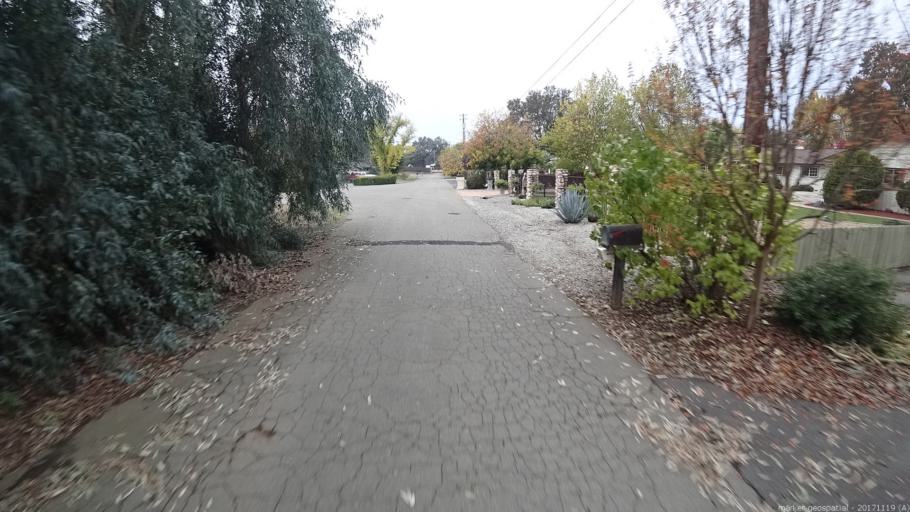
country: US
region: California
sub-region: Shasta County
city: Anderson
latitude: 40.4940
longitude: -122.3494
